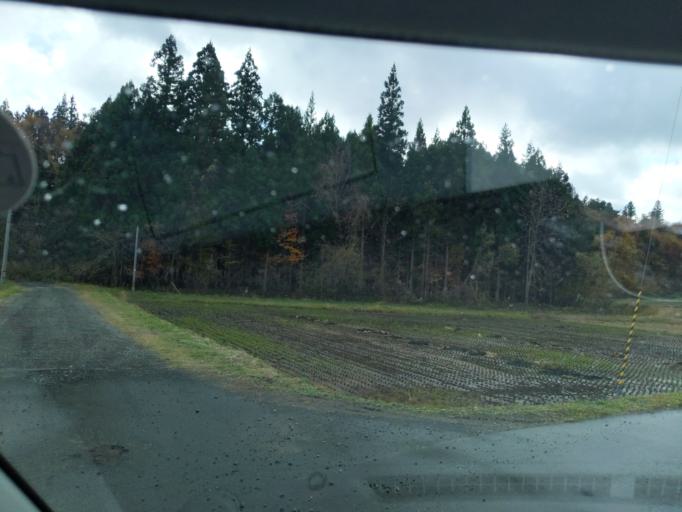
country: JP
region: Iwate
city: Mizusawa
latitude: 39.1185
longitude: 140.9585
